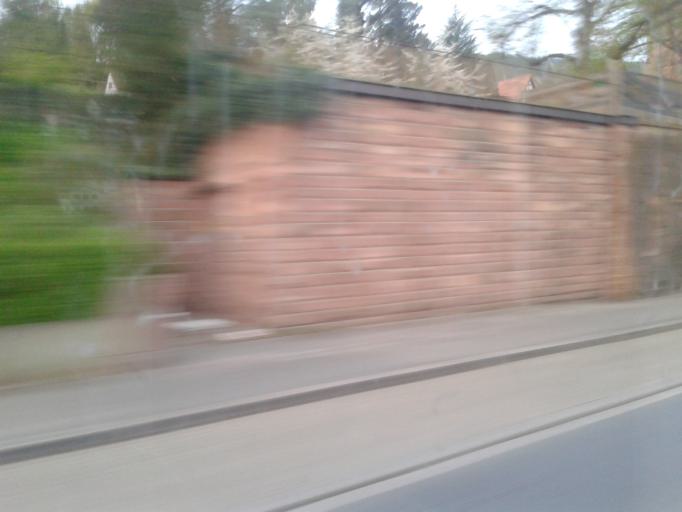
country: DE
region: Baden-Wuerttemberg
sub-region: Karlsruhe Region
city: Gaiberg
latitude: 49.4154
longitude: 8.7505
